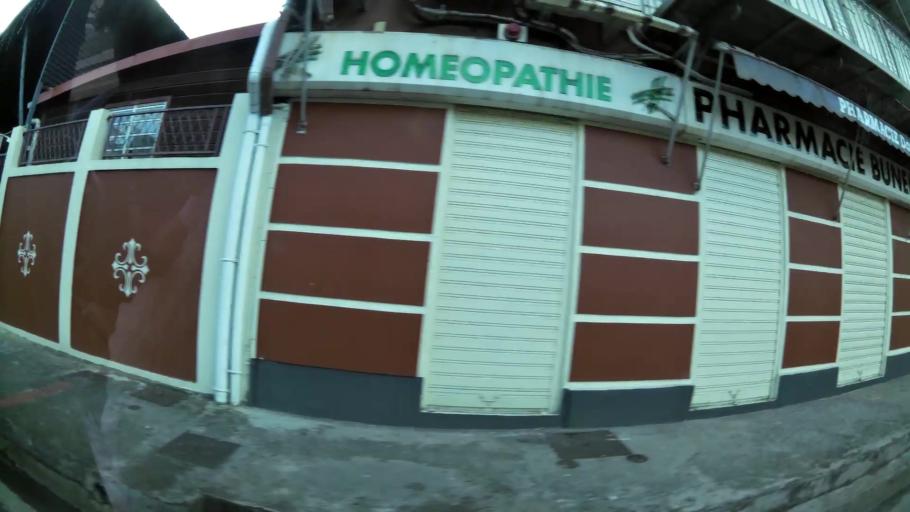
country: GP
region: Guadeloupe
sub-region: Guadeloupe
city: Pointe-a-Pitre
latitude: 16.2377
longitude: -61.5323
